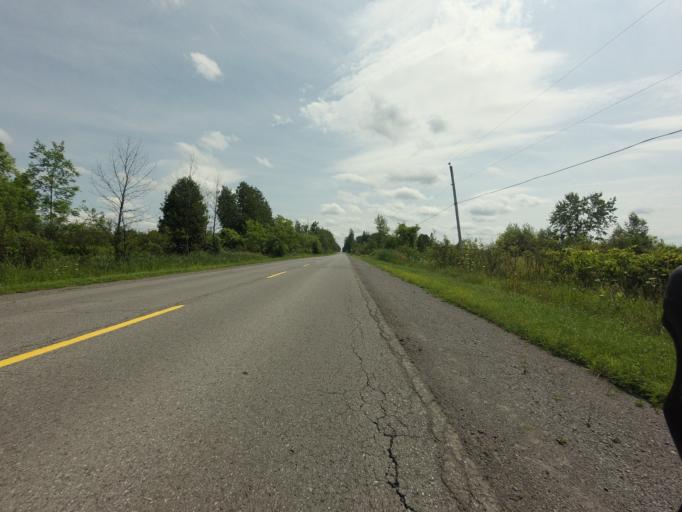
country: CA
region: Ontario
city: Ottawa
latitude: 45.2861
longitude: -75.6318
